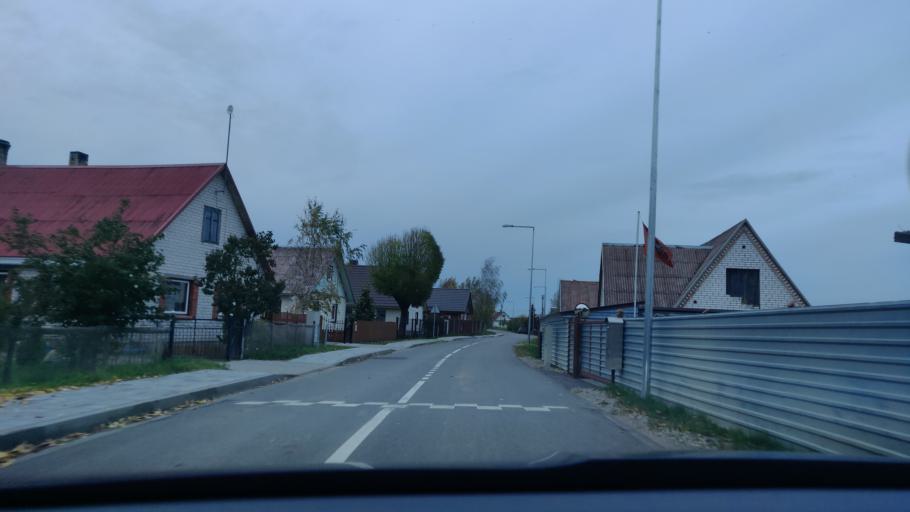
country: LT
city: Lentvaris
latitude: 54.5868
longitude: 25.0512
